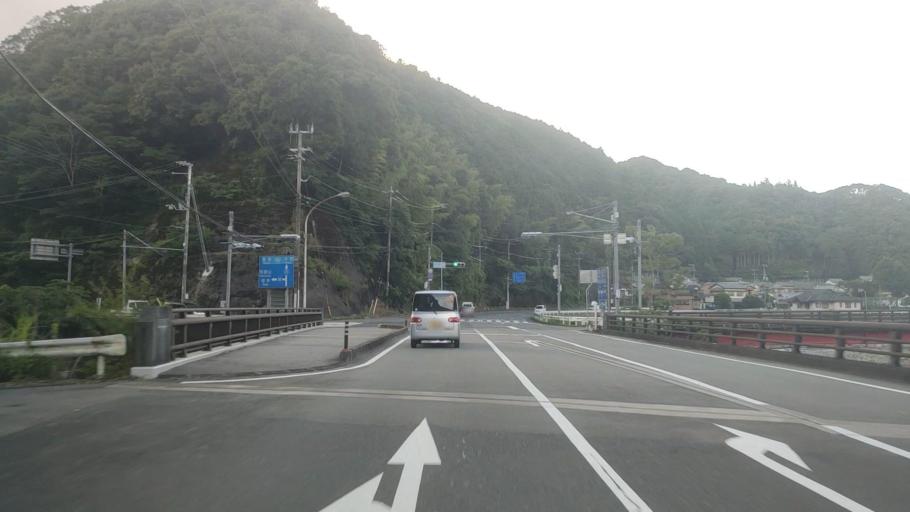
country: JP
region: Wakayama
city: Tanabe
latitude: 33.7877
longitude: 135.5060
